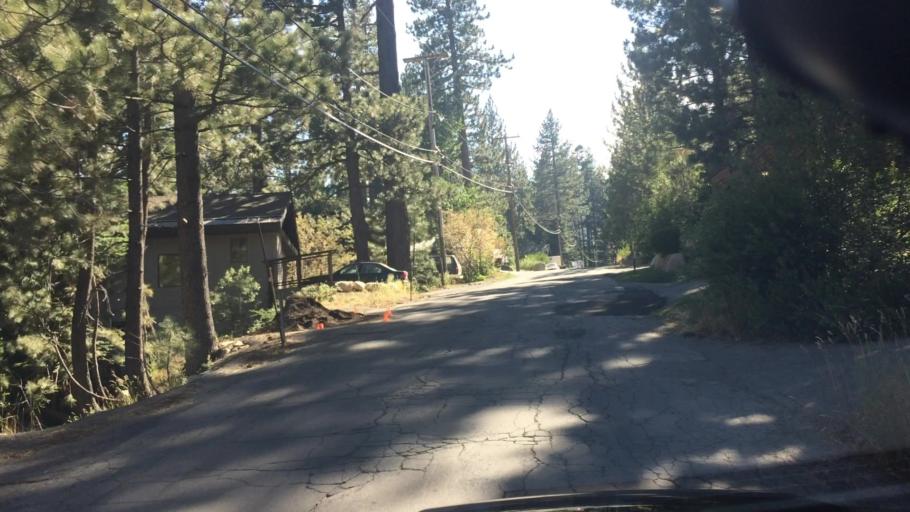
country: US
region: California
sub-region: Placer County
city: Sunnyside-Tahoe City
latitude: 39.2030
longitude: -120.2256
